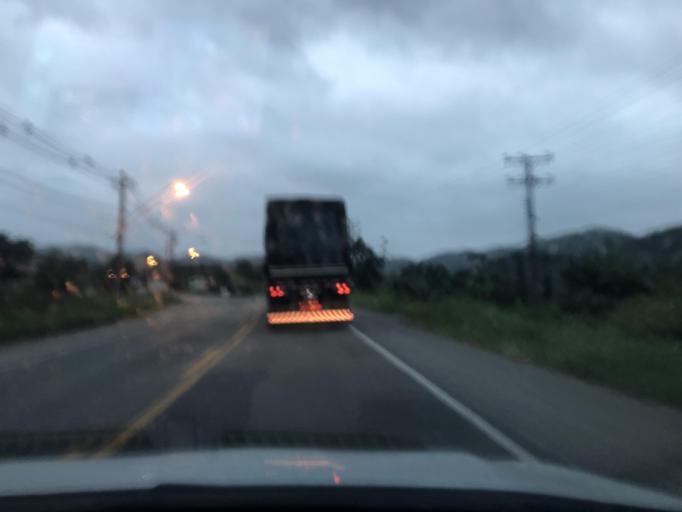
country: BR
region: Santa Catarina
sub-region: Pomerode
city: Pomerode
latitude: -26.7771
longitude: -49.0824
